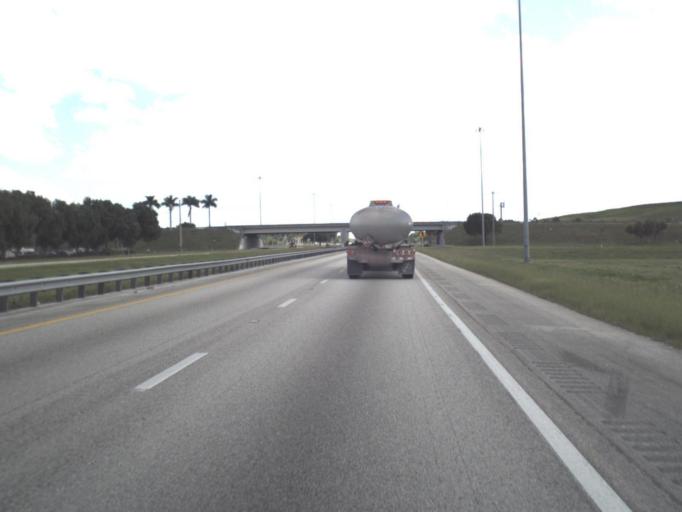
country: US
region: Florida
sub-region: Miami-Dade County
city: Country Club
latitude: 25.9707
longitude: -80.2983
